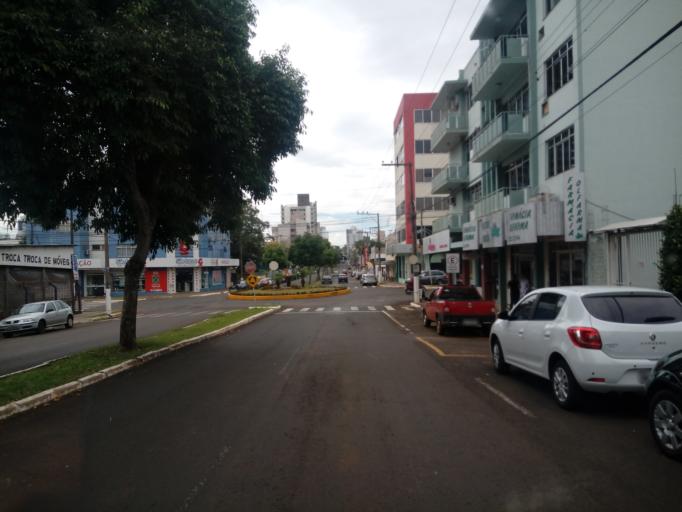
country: BR
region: Santa Catarina
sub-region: Chapeco
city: Chapeco
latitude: -27.1074
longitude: -52.6177
